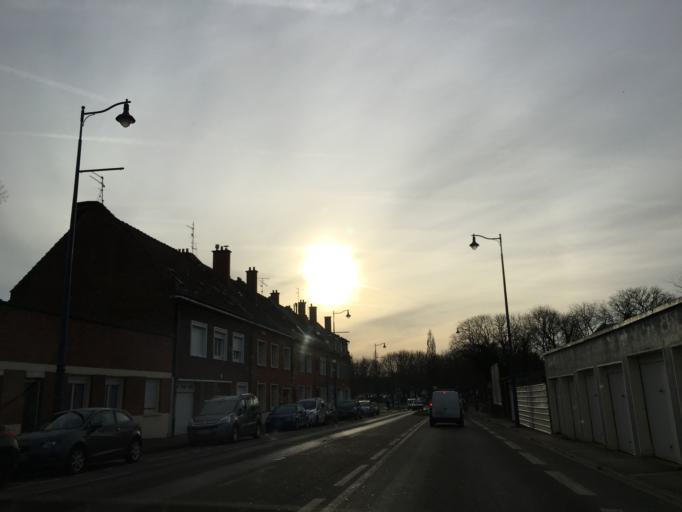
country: FR
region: Nord-Pas-de-Calais
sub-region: Departement du Pas-de-Calais
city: Arras
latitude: 50.2881
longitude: 2.7858
